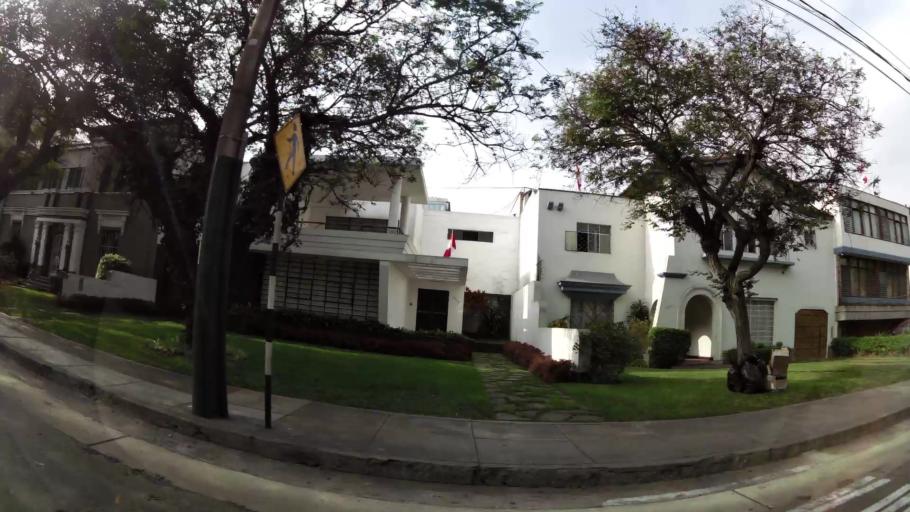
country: PE
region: Lima
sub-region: Lima
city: San Isidro
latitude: -12.0944
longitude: -77.0558
